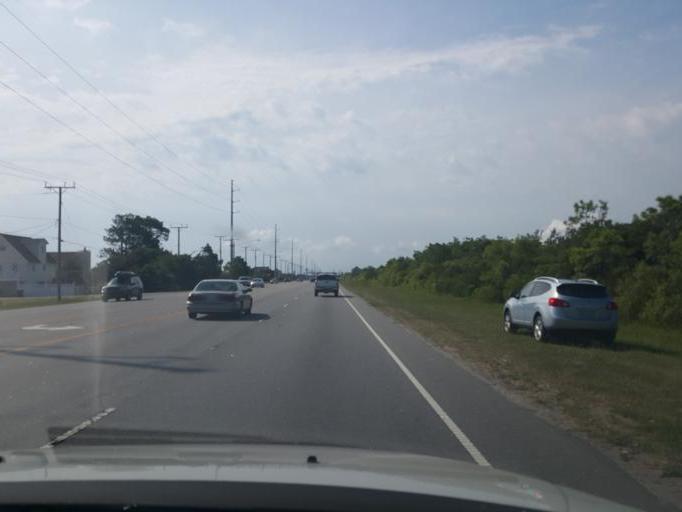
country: US
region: North Carolina
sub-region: Dare County
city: Kill Devil Hills
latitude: 36.0186
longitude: -75.6640
